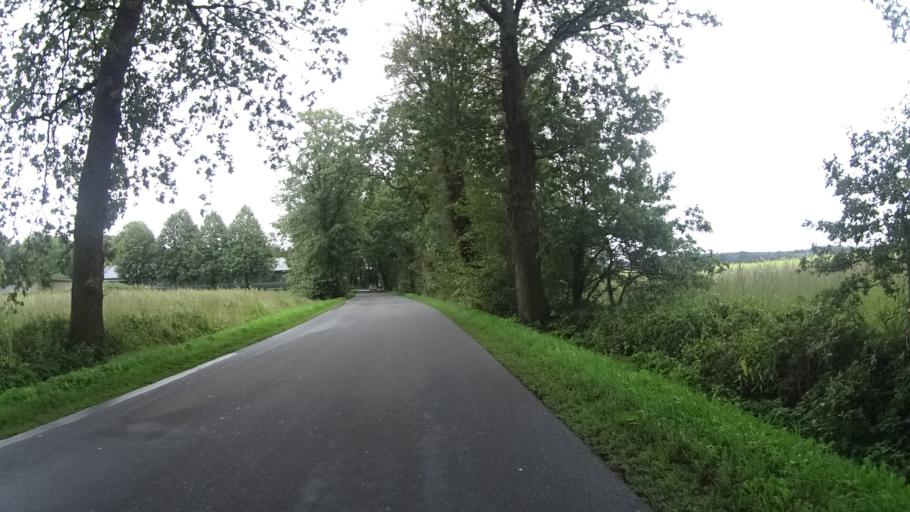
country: DE
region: Schleswig-Holstein
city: Henstedt-Ulzburg
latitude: 53.7768
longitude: 9.9652
